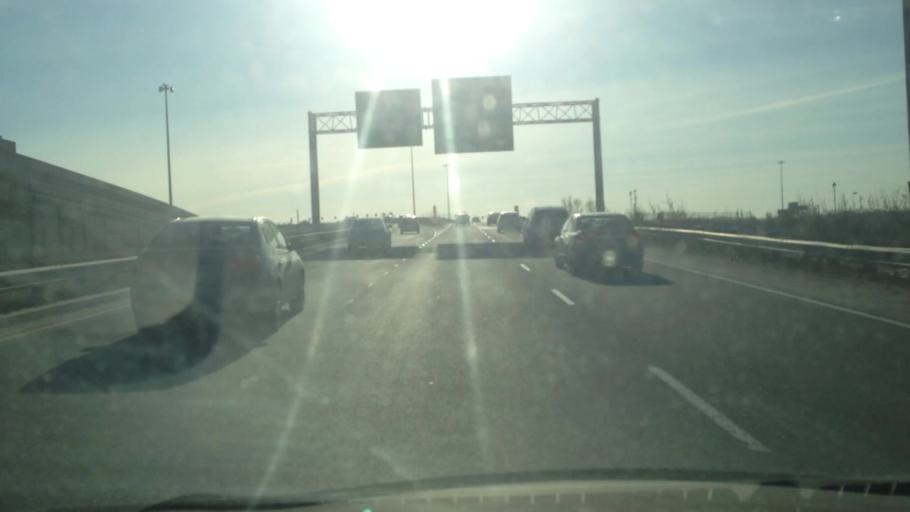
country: CA
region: Quebec
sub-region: Laurentides
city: Boisbriand
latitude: 45.6288
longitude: -73.8440
